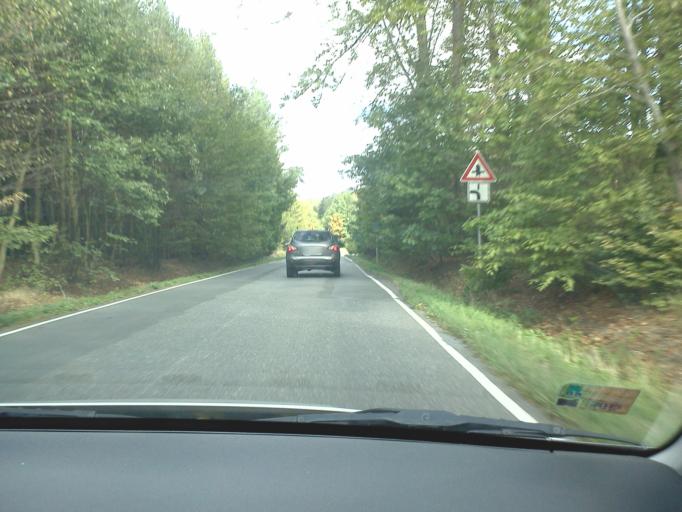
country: CZ
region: Central Bohemia
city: Kostelec nad Cernymi Lesy
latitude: 50.0279
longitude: 14.8065
